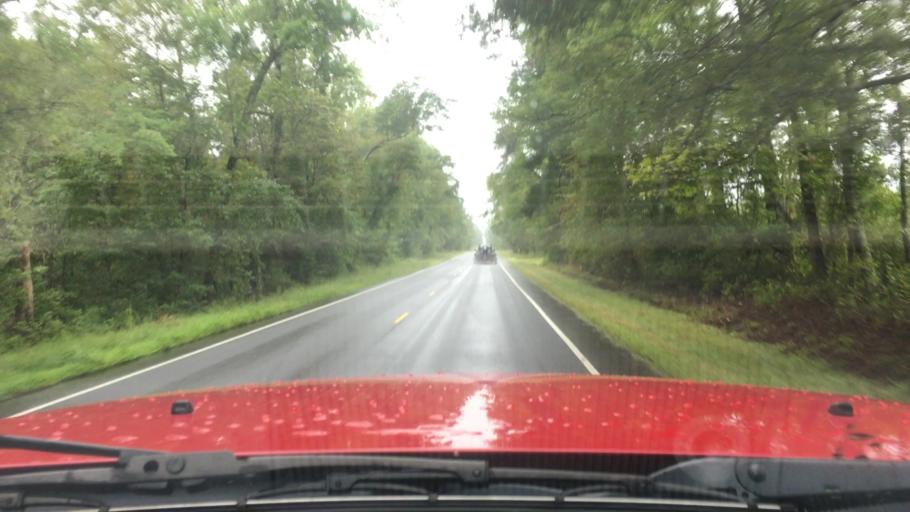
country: US
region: Virginia
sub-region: Caroline County
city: Bowling Green
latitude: 37.9704
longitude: -77.3415
